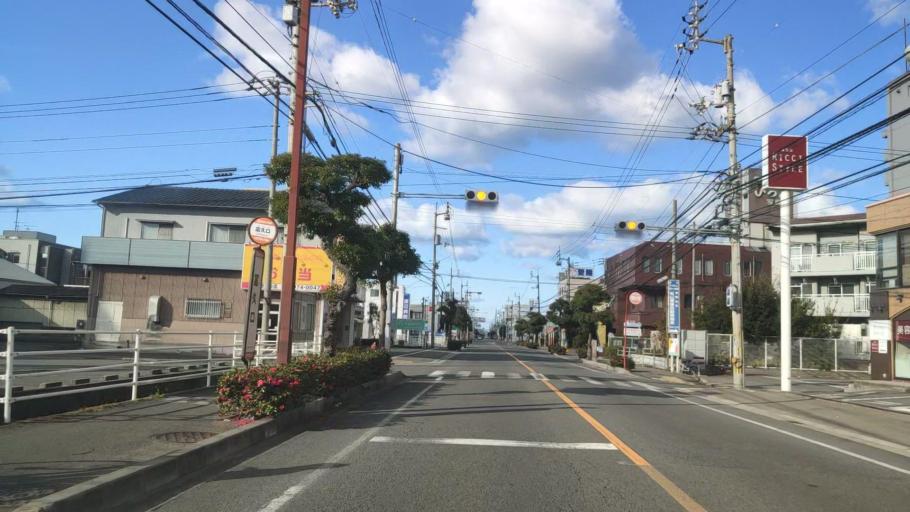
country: JP
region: Ehime
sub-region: Shikoku-chuo Shi
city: Matsuyama
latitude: 33.8284
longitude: 132.7280
